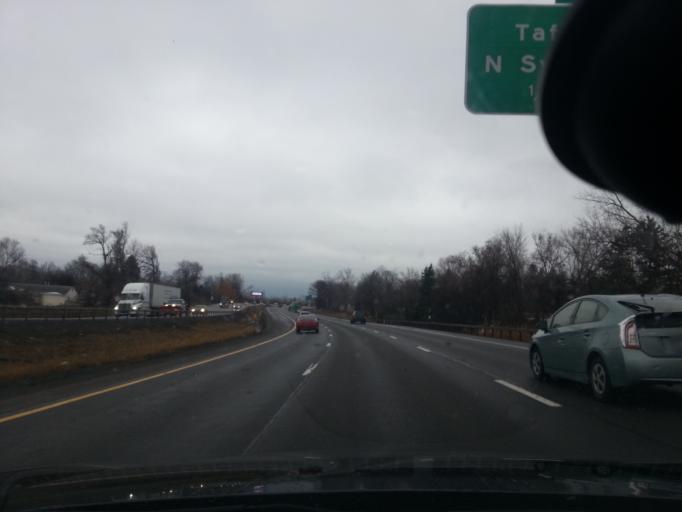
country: US
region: New York
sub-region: Onondaga County
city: North Syracuse
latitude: 43.1341
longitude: -76.1197
